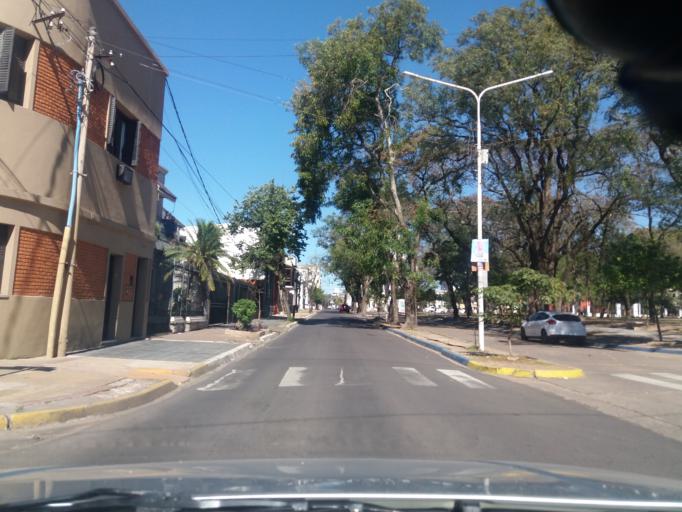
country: AR
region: Corrientes
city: Corrientes
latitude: -27.4707
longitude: -58.8394
